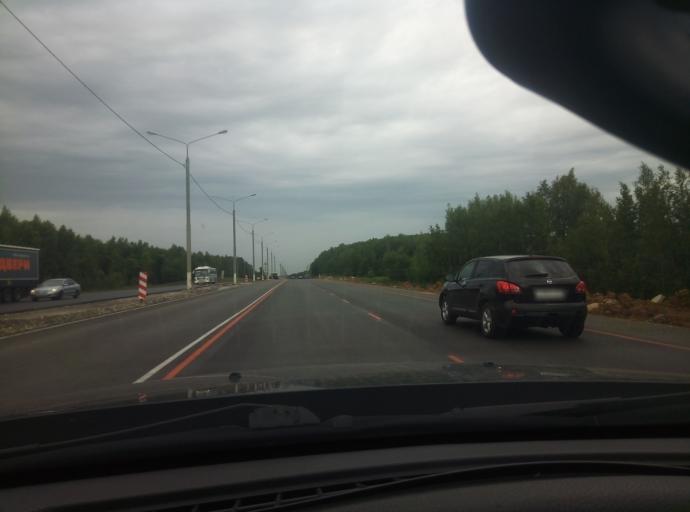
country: RU
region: Tula
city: Yasnogorsk
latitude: 54.5464
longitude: 37.5177
